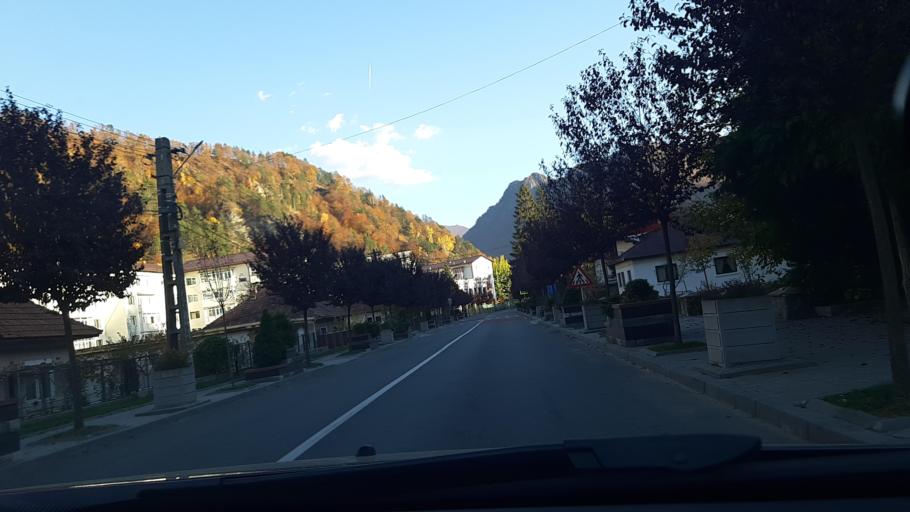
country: RO
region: Valcea
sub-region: Comuna Brezoi
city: Brezoi
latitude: 45.3436
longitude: 24.2443
